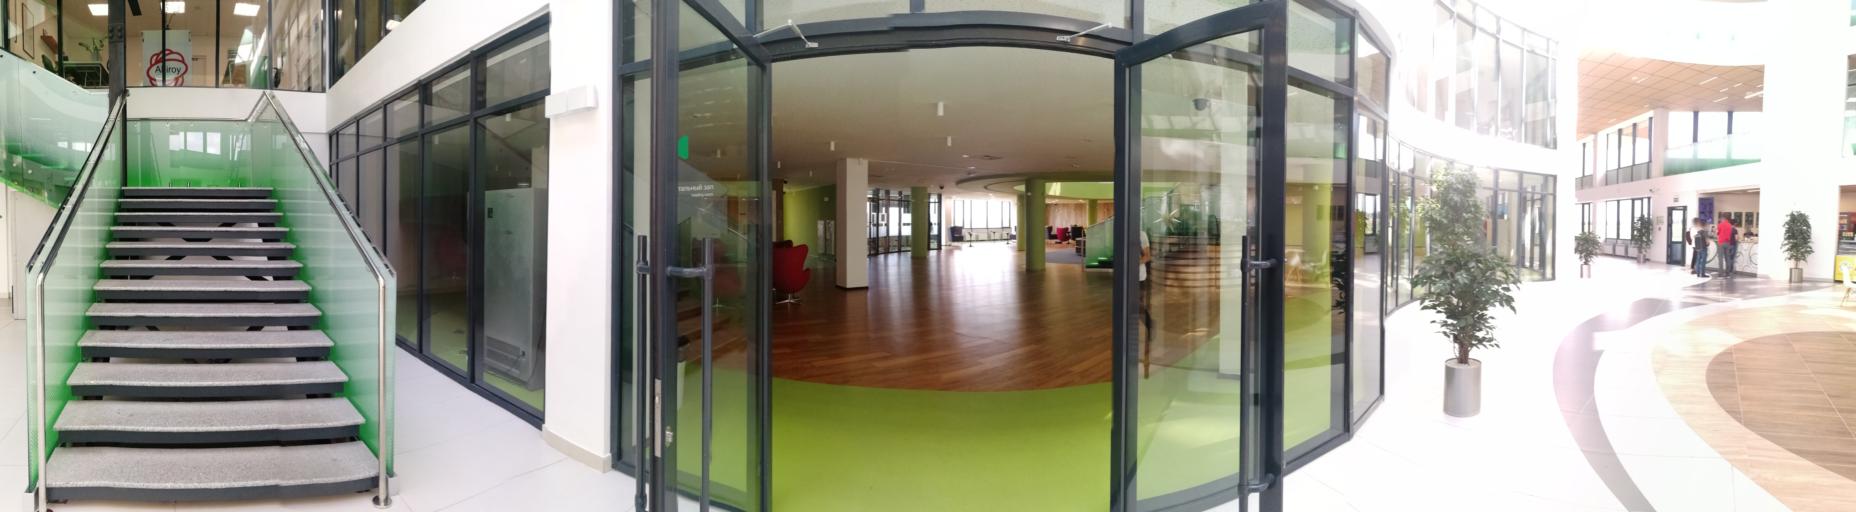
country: RU
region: Tatarstan
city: Sviyazhsk
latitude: 55.7536
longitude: 48.7433
